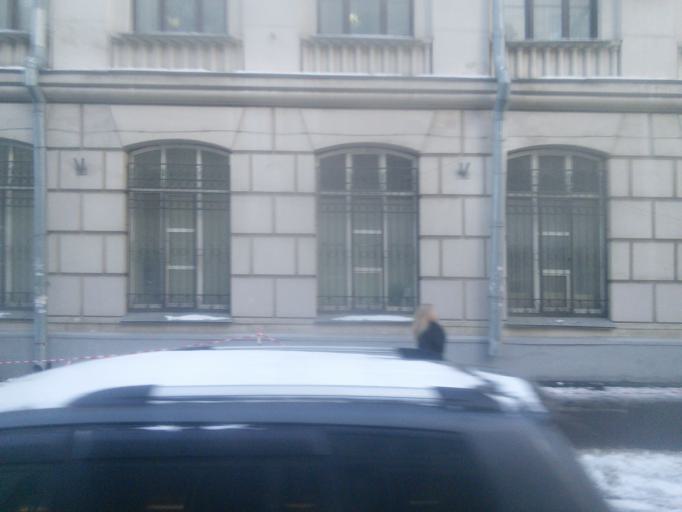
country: RU
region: Moscow
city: Lefortovo
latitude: 55.7645
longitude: 37.6825
